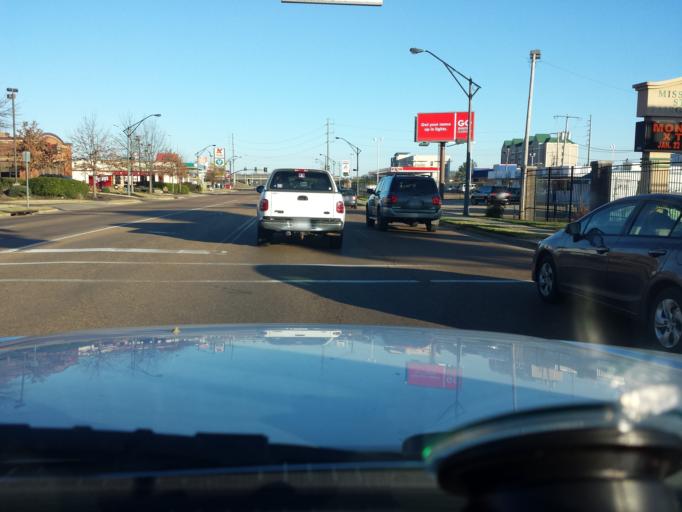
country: US
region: Mississippi
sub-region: Hinds County
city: Jackson
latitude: 32.3035
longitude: -90.1716
